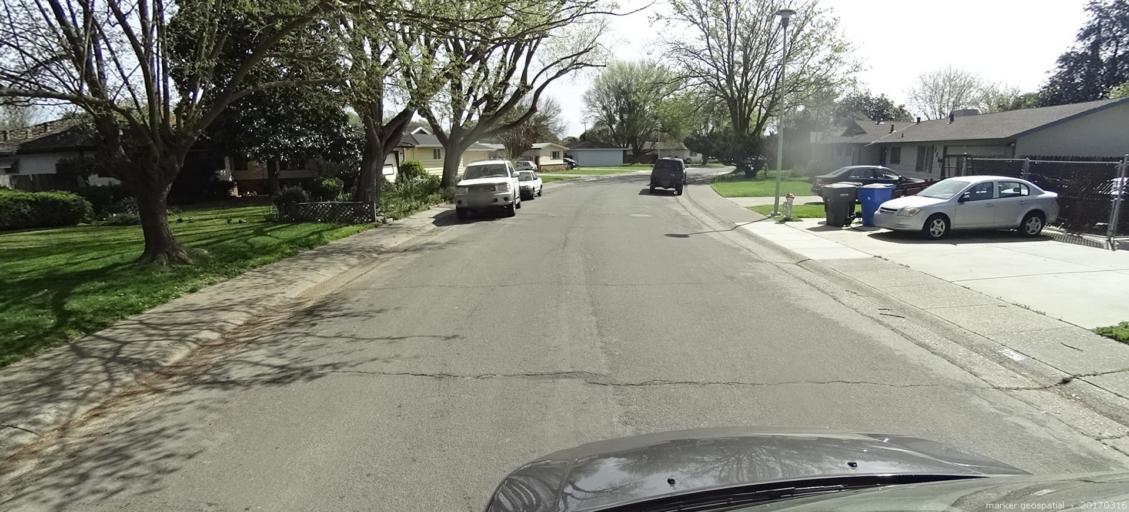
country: US
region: California
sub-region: Sacramento County
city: Parkway
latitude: 38.4981
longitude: -121.5038
